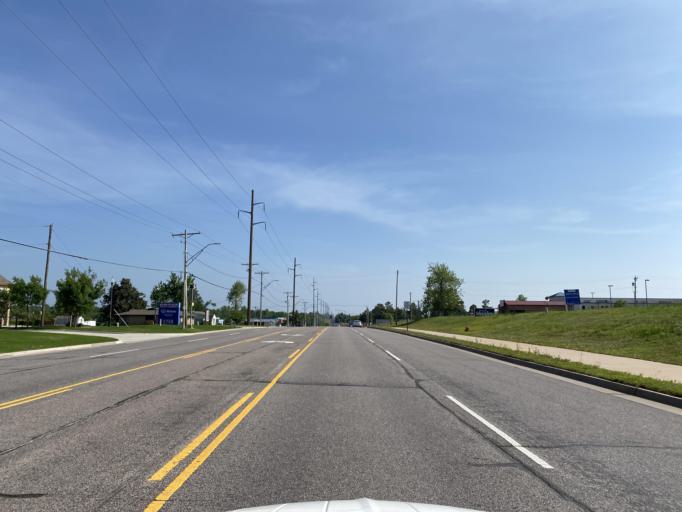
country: US
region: Oklahoma
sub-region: Oklahoma County
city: Midwest City
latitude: 35.4377
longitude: -97.3532
